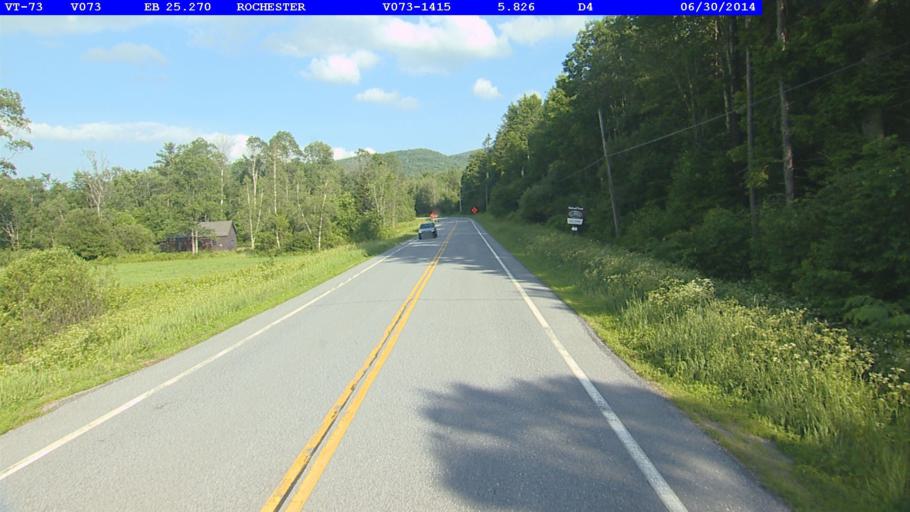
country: US
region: Vermont
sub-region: Orange County
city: Randolph
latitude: 43.8498
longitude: -72.8596
